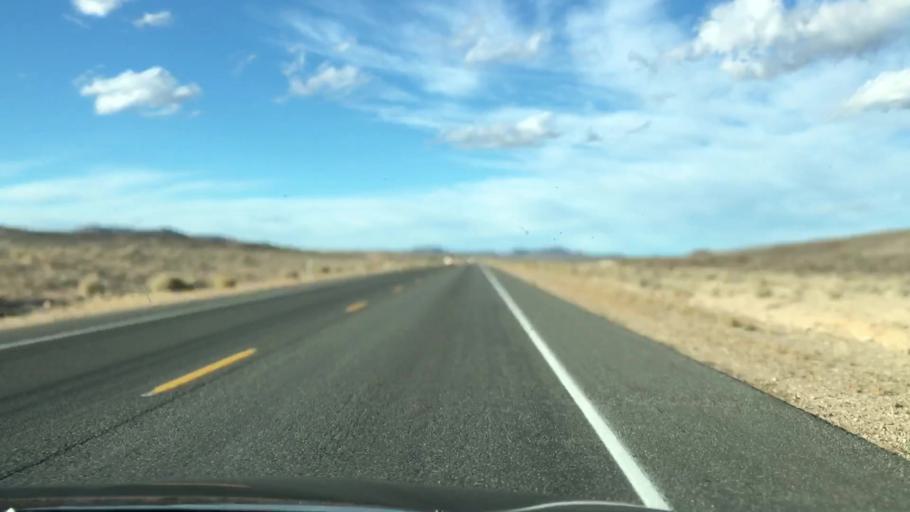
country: US
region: Nevada
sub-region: Esmeralda County
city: Goldfield
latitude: 37.5352
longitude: -117.1936
